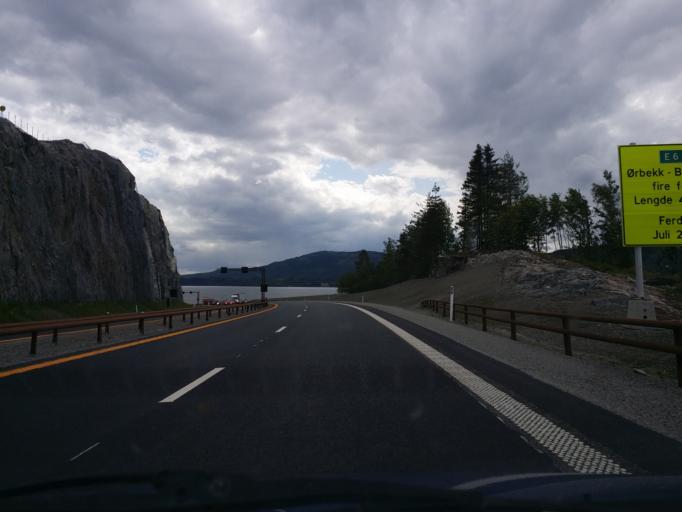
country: NO
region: Akershus
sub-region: Eidsvoll
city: Eidsvoll
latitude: 60.4594
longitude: 11.2412
